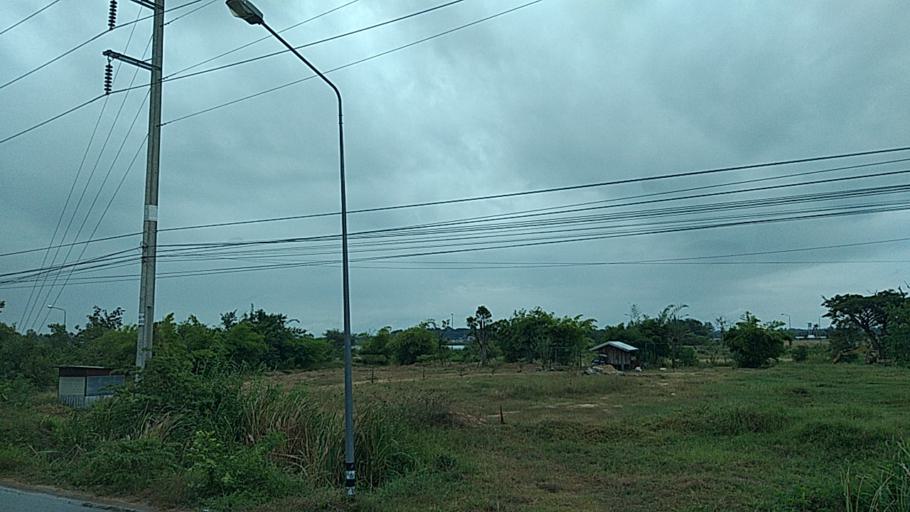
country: TH
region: Maha Sarakham
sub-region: Amphoe Borabue
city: Borabue
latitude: 16.0416
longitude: 103.1281
